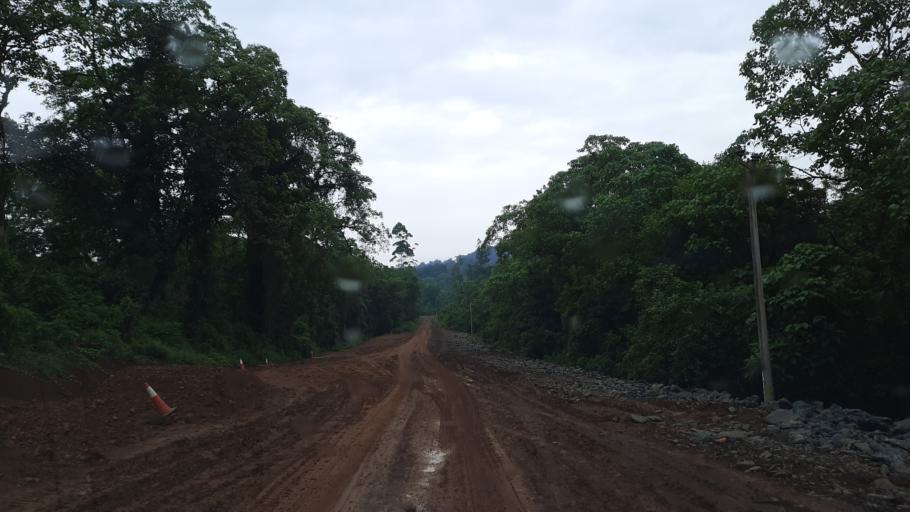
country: ET
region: Oromiya
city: Gore
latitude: 7.8686
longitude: 35.4801
